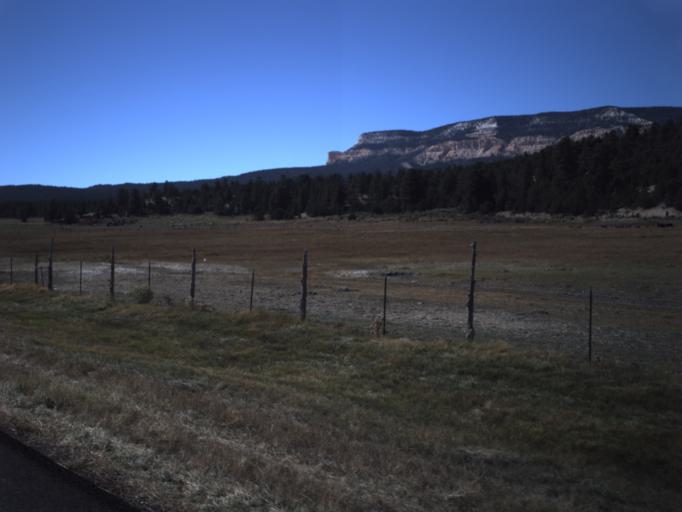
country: US
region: Utah
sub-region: Garfield County
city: Panguitch
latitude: 37.6886
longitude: -111.8048
